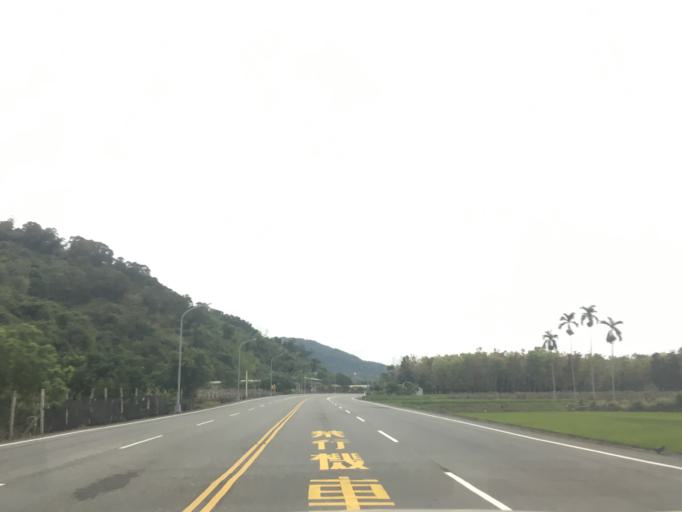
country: TW
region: Taiwan
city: Taitung City
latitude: 22.7379
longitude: 121.0566
